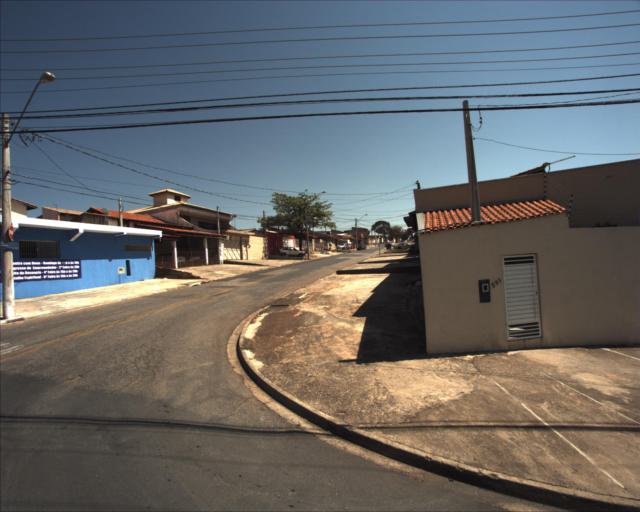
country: BR
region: Sao Paulo
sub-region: Sorocaba
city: Sorocaba
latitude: -23.4733
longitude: -47.4824
